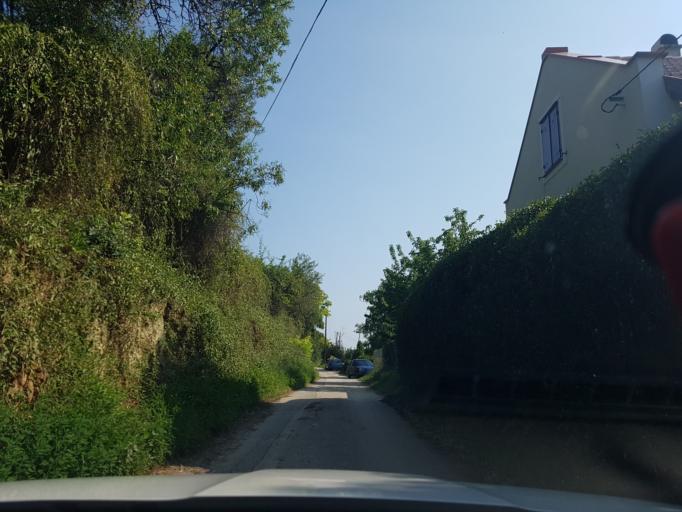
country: HU
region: Veszprem
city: Balatonalmadi
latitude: 46.9993
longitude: 17.9853
